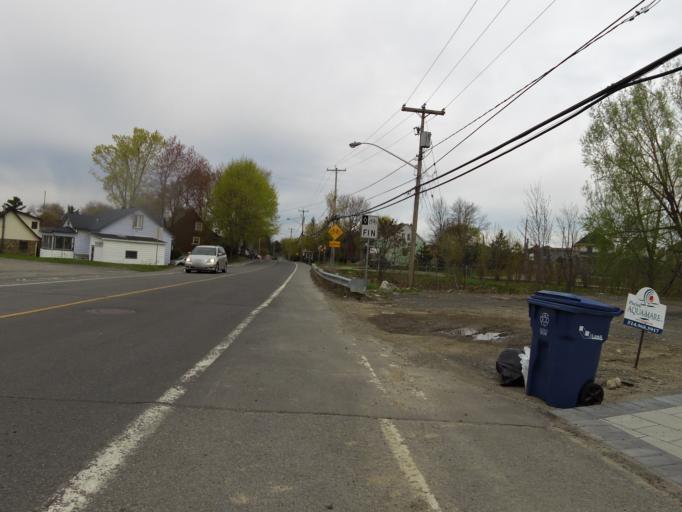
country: CA
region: Quebec
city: Dollard-Des Ormeaux
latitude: 45.5208
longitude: -73.8325
